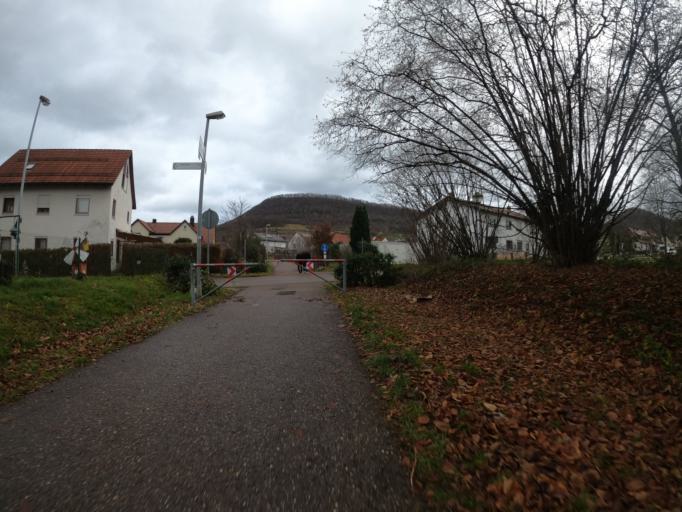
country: DE
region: Baden-Wuerttemberg
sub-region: Regierungsbezirk Stuttgart
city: Donzdorf
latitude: 48.6835
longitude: 9.8132
